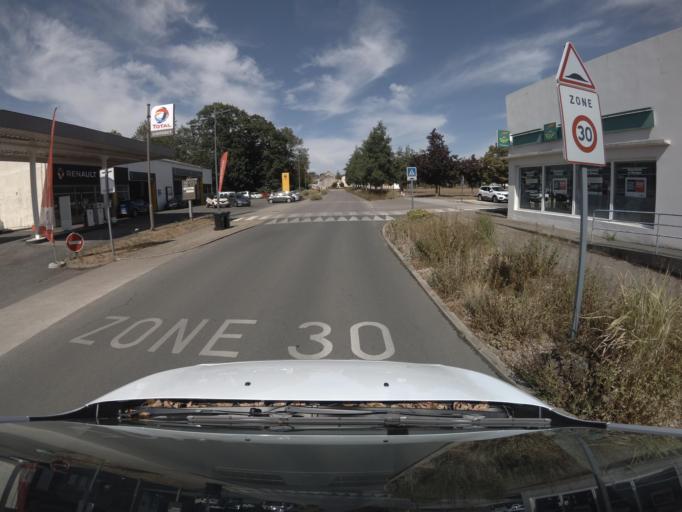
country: FR
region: Poitou-Charentes
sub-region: Departement des Deux-Sevres
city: Nueil-les-Aubiers
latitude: 46.9507
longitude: -0.5928
